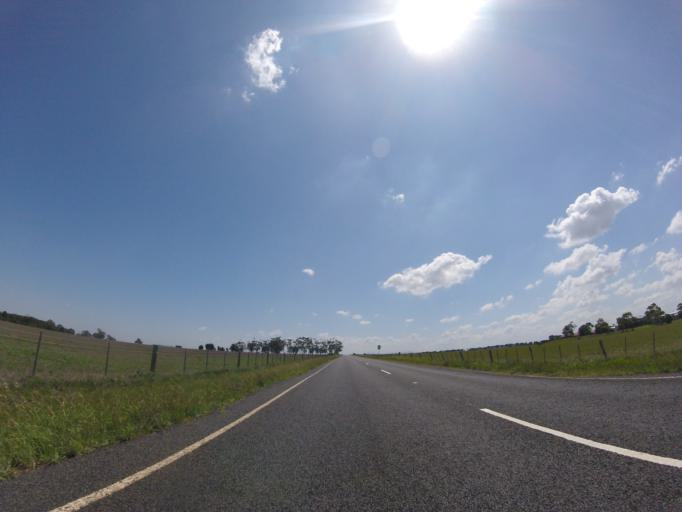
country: AU
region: Victoria
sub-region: Hume
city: Greenvale
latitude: -37.6189
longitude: 144.8185
